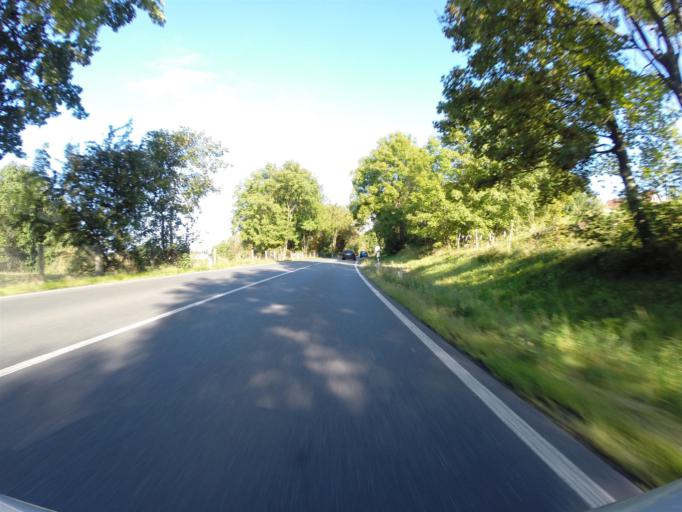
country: DE
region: Thuringia
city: Grossschwabhausen
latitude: 50.9572
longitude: 11.5209
